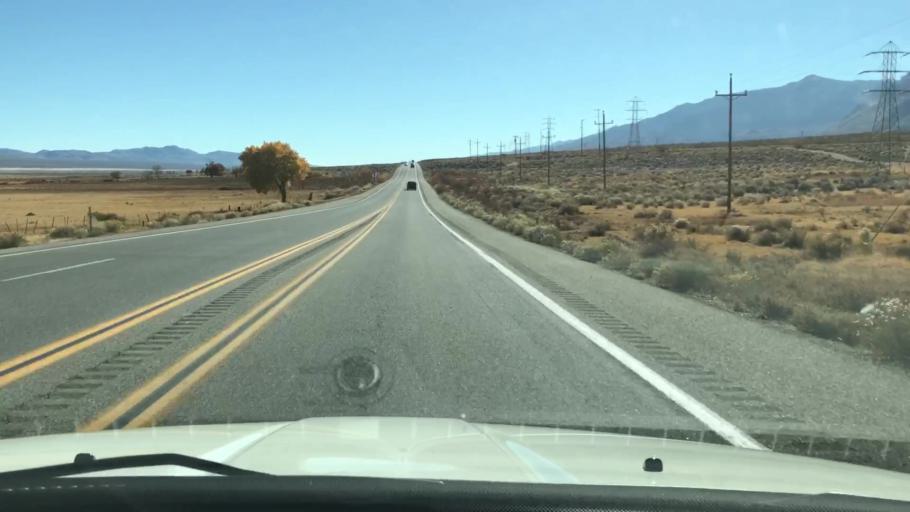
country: US
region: California
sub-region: Inyo County
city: Lone Pine
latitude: 36.3492
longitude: -118.0228
